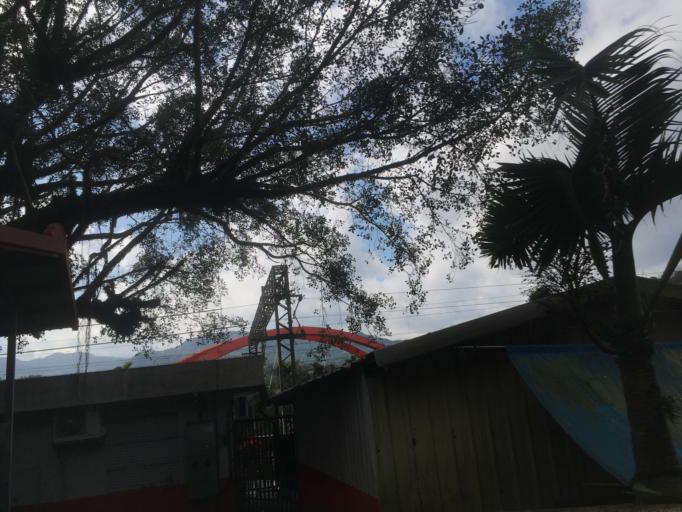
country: TW
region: Taiwan
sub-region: Keelung
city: Keelung
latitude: 25.0220
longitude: 121.9096
